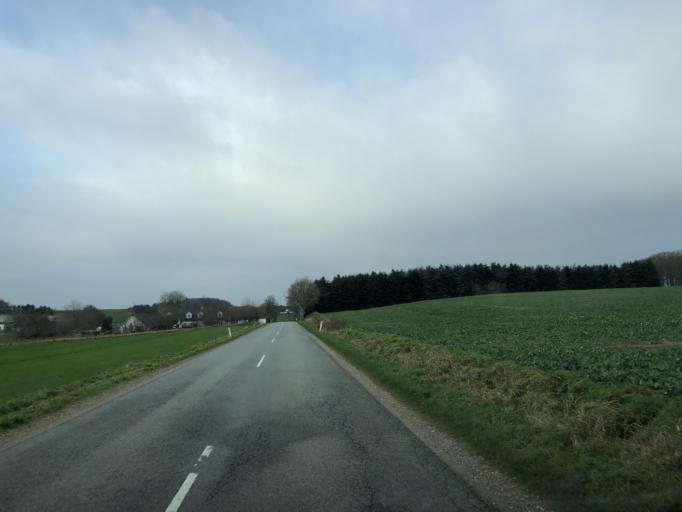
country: DK
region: North Denmark
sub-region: Rebild Kommune
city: Stovring
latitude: 56.9174
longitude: 9.7864
